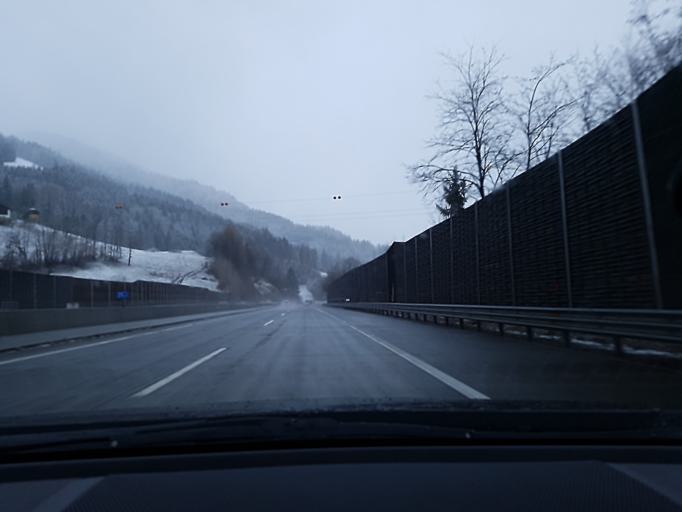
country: AT
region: Salzburg
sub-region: Politischer Bezirk Hallein
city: Kuchl
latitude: 47.6114
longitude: 13.1427
